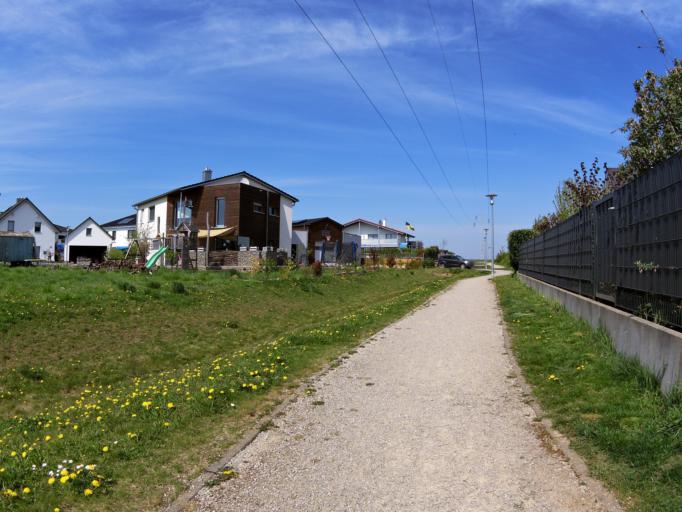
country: DE
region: Bavaria
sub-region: Regierungsbezirk Unterfranken
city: Unterpleichfeld
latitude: 49.8721
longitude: 10.0402
